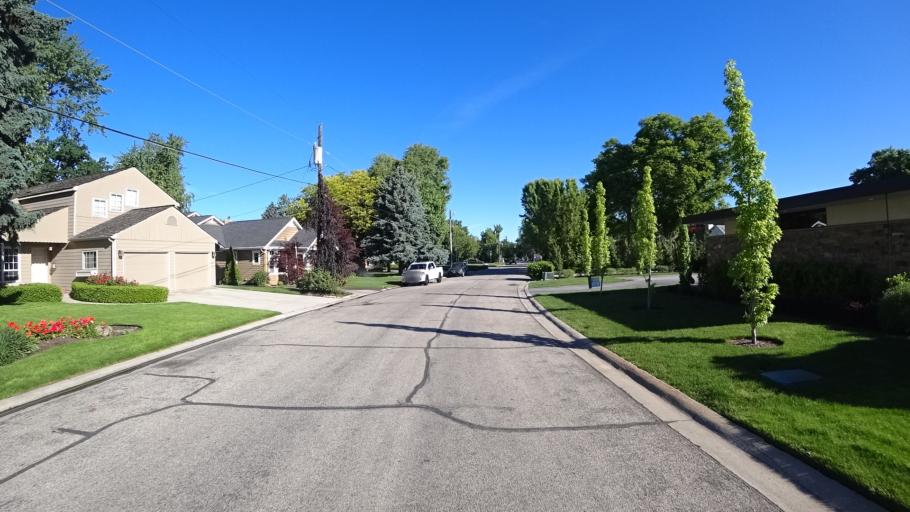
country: US
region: Idaho
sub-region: Ada County
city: Garden City
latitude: 43.6131
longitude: -116.2297
